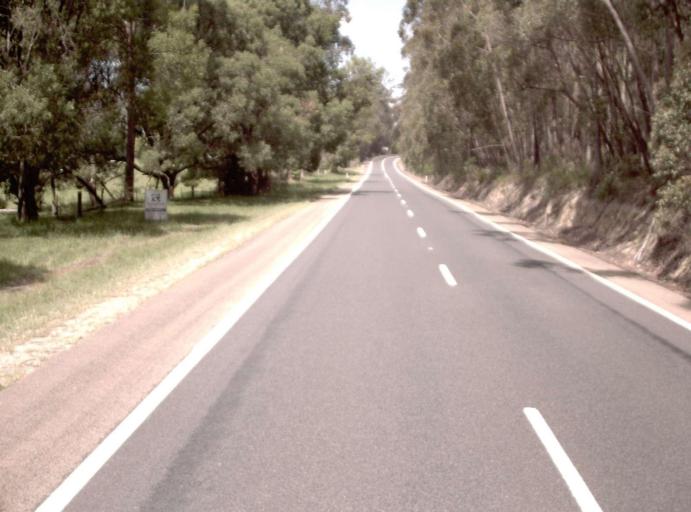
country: AU
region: New South Wales
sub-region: Bombala
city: Bombala
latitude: -37.5363
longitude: 149.3920
